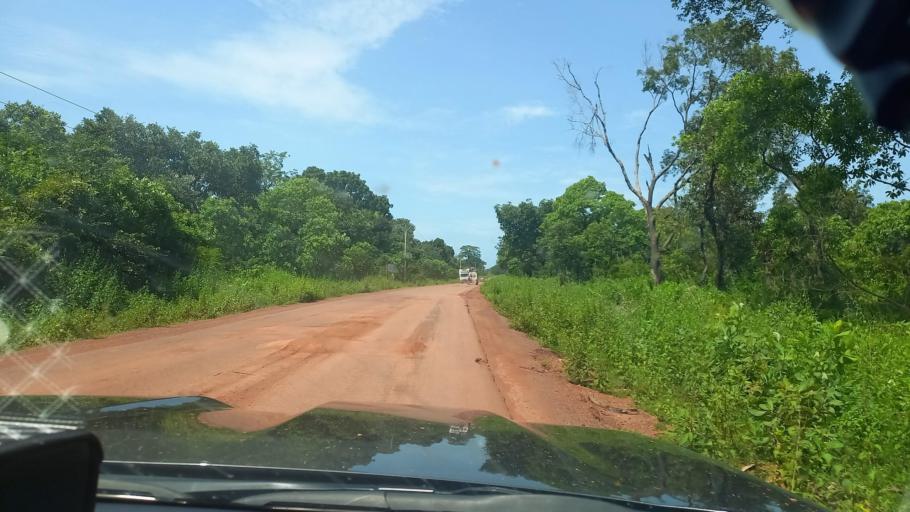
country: SN
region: Kolda
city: Marsassoum
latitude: 12.8576
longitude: -16.0938
